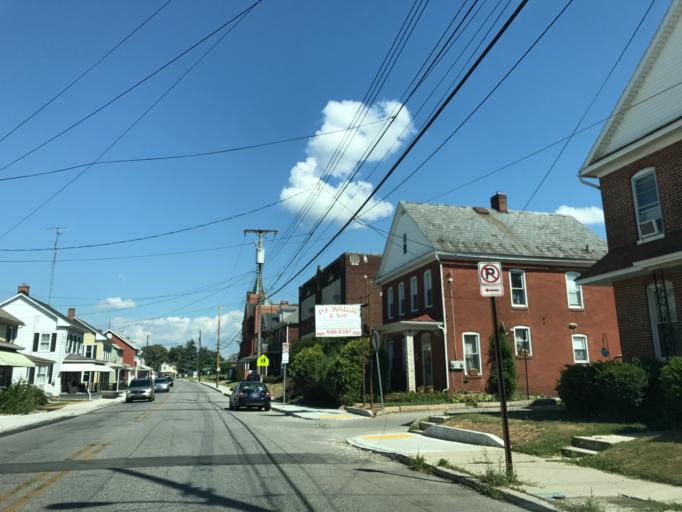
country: US
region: Pennsylvania
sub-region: Adams County
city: Midway
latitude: 39.8049
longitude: -76.9966
